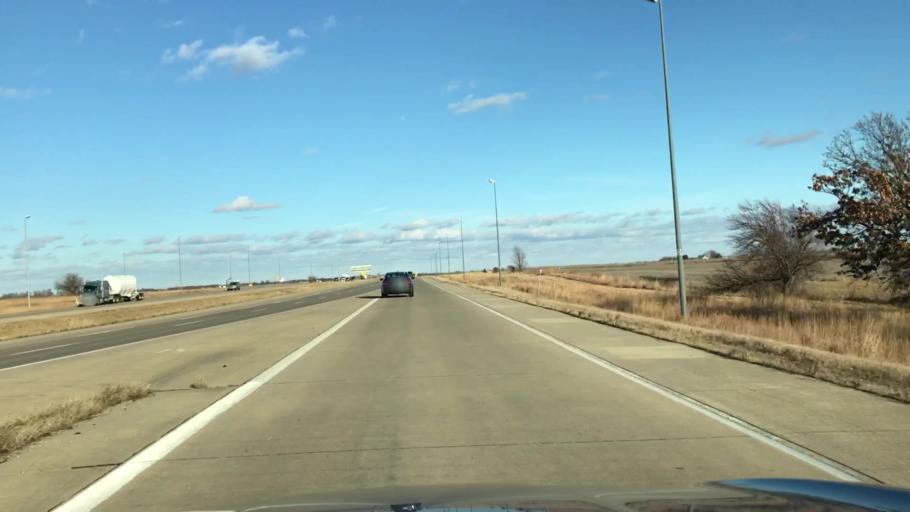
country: US
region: Illinois
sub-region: McLean County
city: Normal
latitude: 40.5378
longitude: -88.9433
